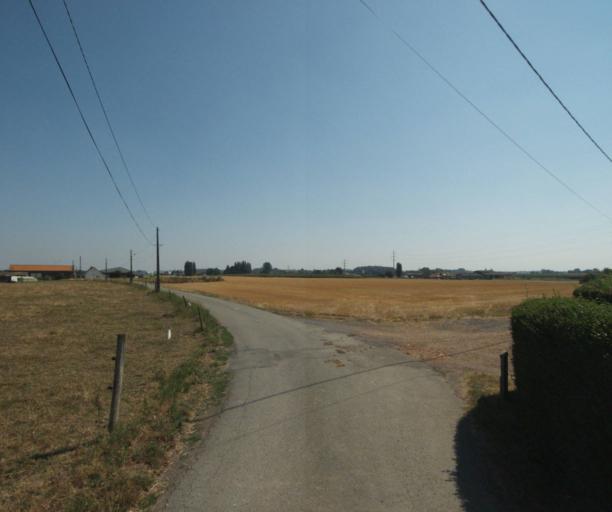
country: FR
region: Nord-Pas-de-Calais
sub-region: Departement du Nord
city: Bousbecque
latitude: 50.7621
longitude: 3.0652
